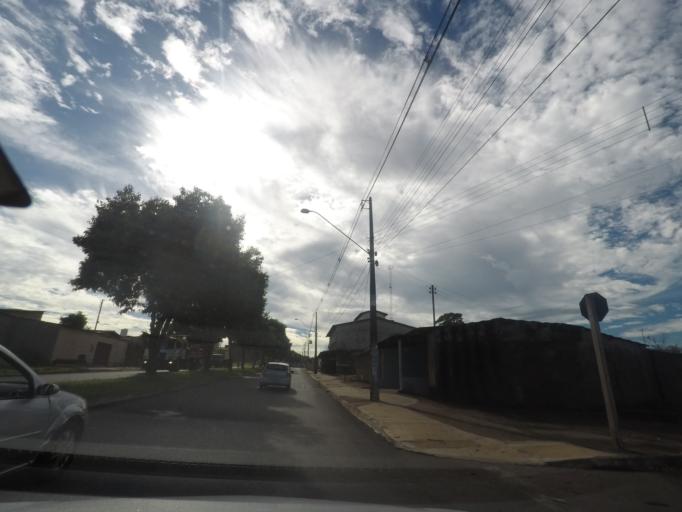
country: BR
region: Goias
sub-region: Aparecida De Goiania
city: Aparecida de Goiania
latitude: -16.8182
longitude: -49.3009
